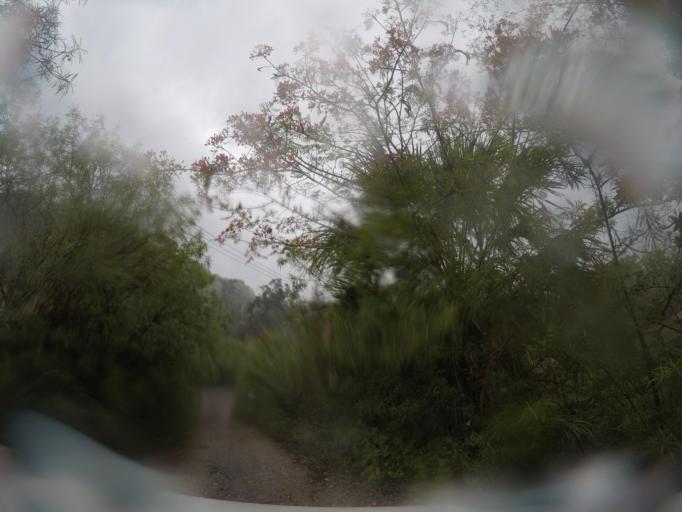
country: TL
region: Baucau
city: Venilale
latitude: -8.6418
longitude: 126.4348
